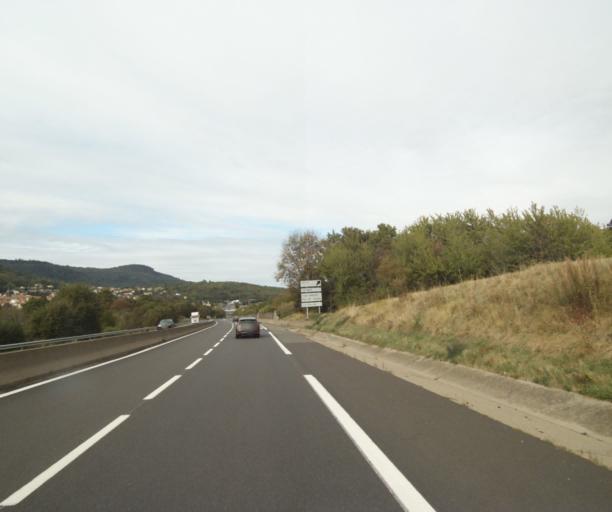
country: FR
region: Auvergne
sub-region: Departement du Puy-de-Dome
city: Ceyrat
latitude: 45.7259
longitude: 3.0716
